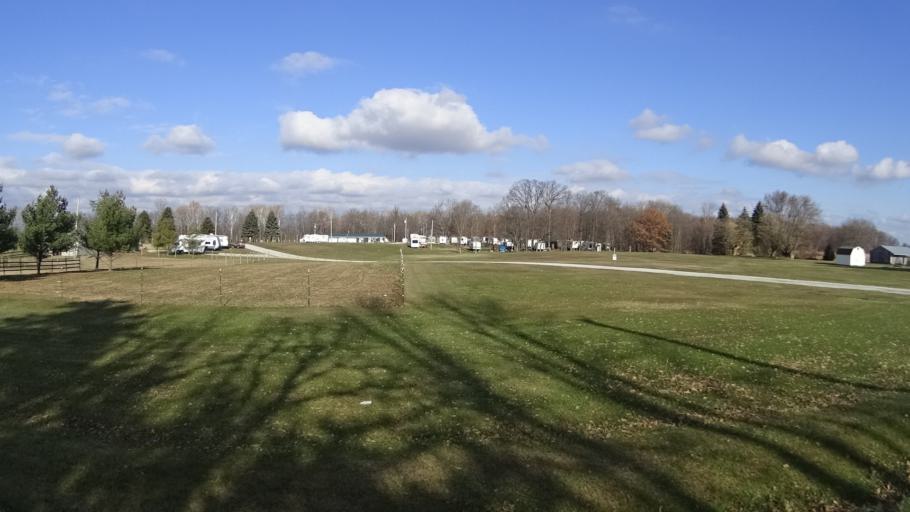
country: US
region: Ohio
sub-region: Lorain County
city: Camden
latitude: 41.2376
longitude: -82.3152
